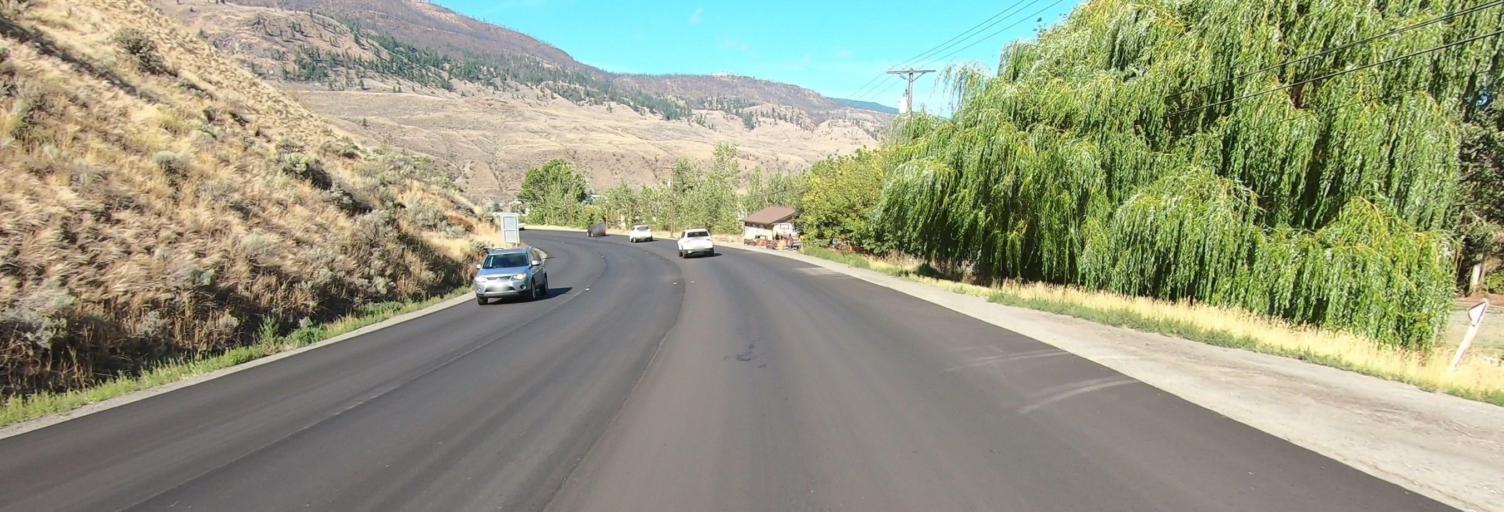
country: CA
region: British Columbia
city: Cache Creek
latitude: 50.8118
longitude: -121.3183
